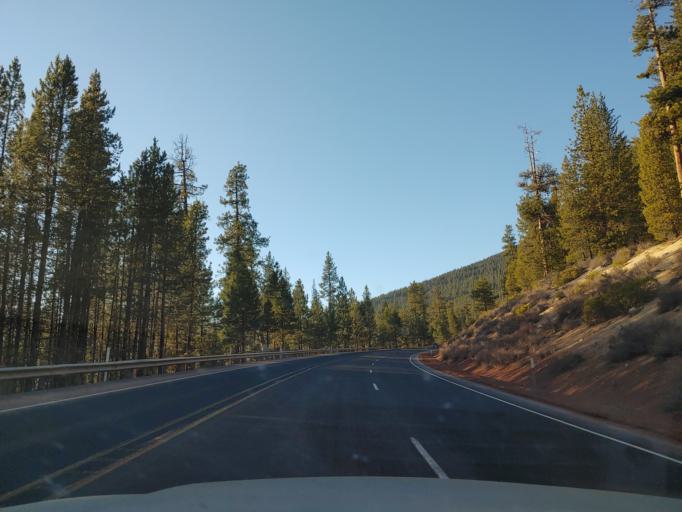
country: US
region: Oregon
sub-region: Deschutes County
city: La Pine
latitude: 43.4446
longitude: -121.8697
